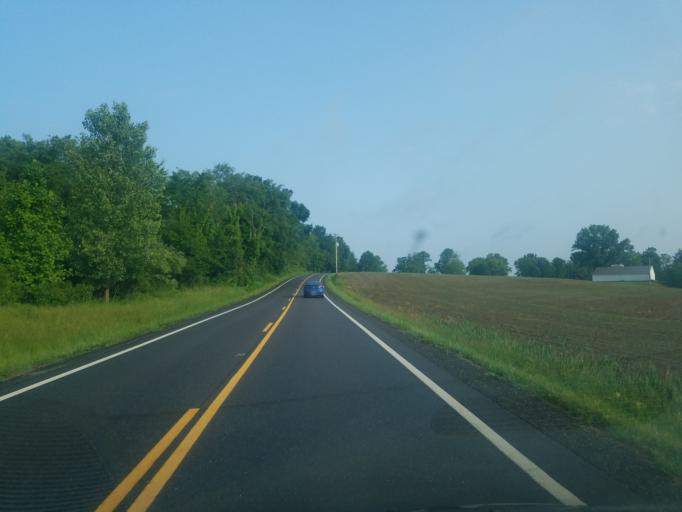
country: US
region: Ohio
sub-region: Tuscarawas County
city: Rockford
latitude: 40.5568
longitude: -81.3287
